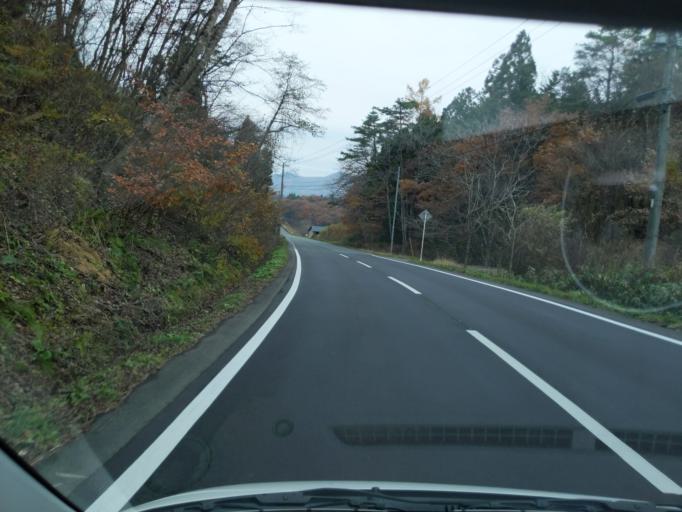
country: JP
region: Iwate
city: Kitakami
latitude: 39.2445
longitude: 141.2186
